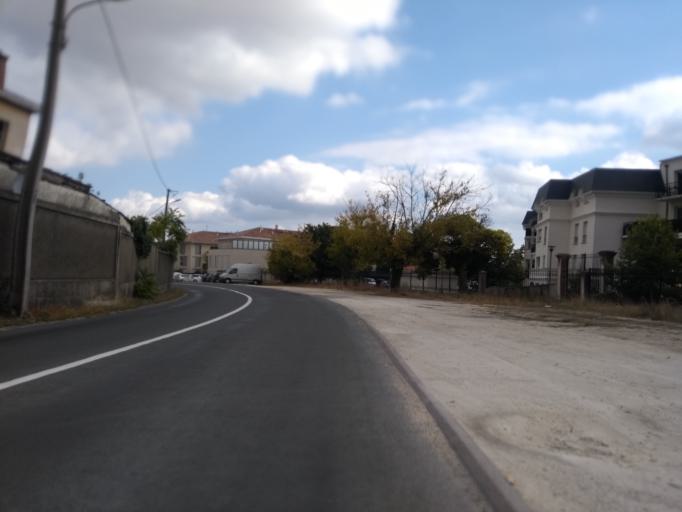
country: FR
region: Aquitaine
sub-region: Departement de la Gironde
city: Talence
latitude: 44.7964
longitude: -0.5746
